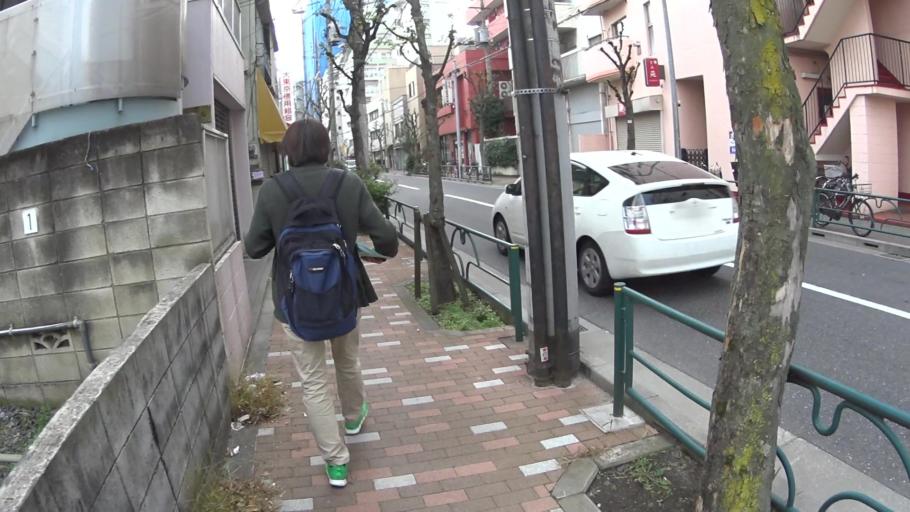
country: JP
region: Tokyo
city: Tokyo
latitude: 35.7252
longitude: 139.7771
